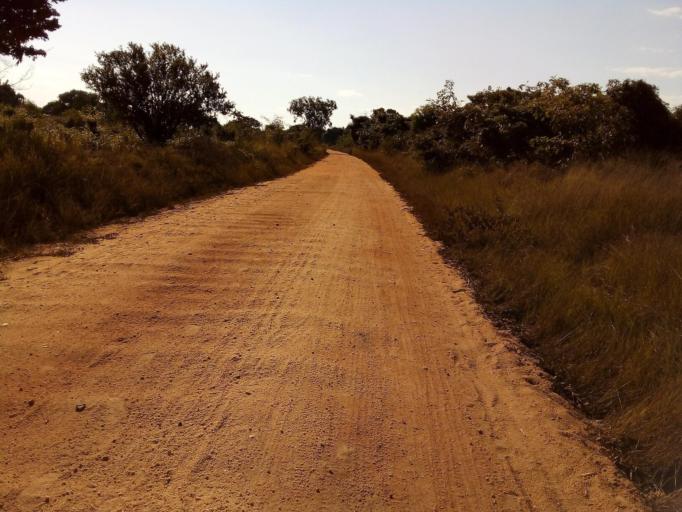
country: MZ
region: Zambezia
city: Quelimane
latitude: -17.5432
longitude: 36.6267
